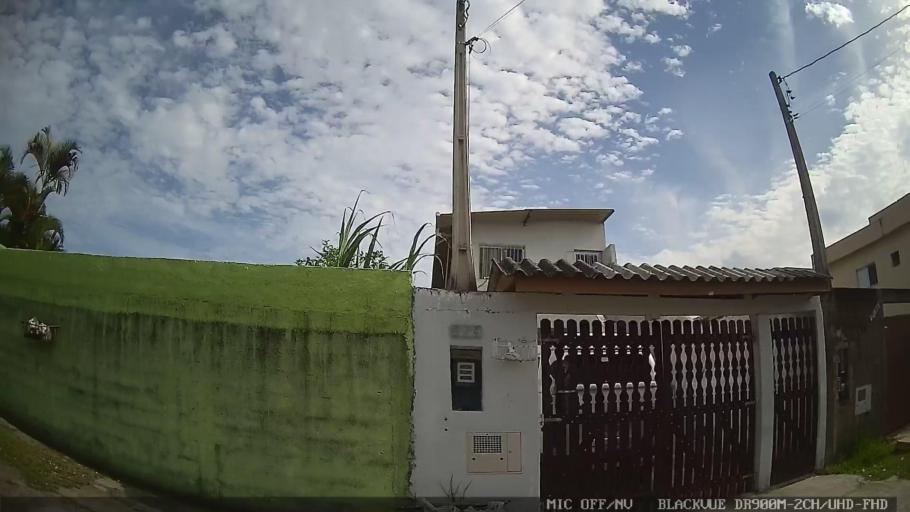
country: BR
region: Sao Paulo
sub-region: Itanhaem
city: Itanhaem
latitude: -24.1627
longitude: -46.7634
